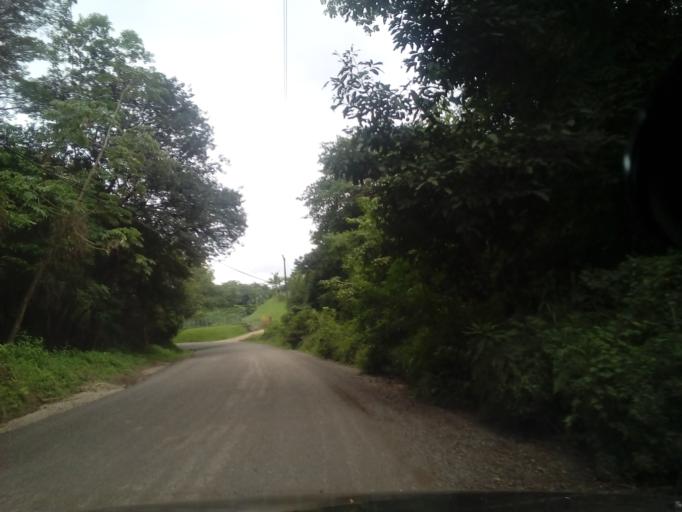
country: CR
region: Guanacaste
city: Samara
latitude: 9.9196
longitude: -85.5383
